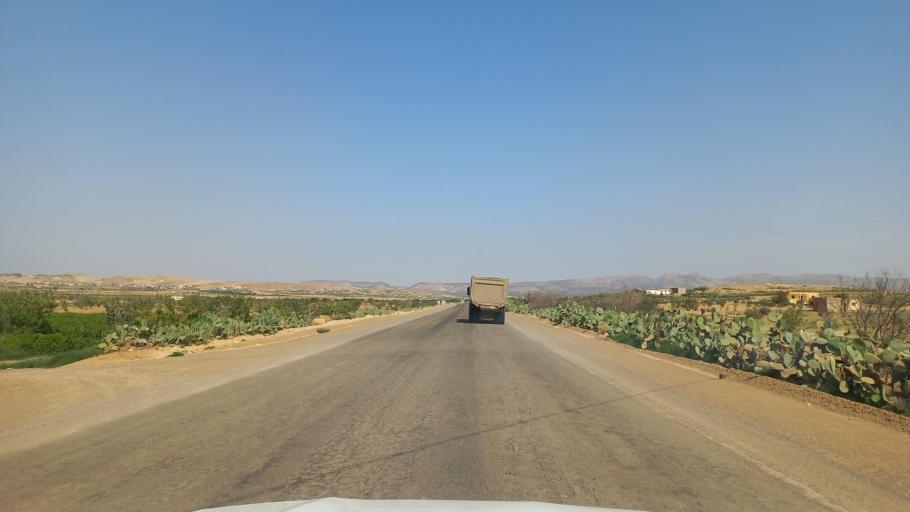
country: TN
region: Al Qasrayn
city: Sbiba
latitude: 35.3589
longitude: 9.0461
